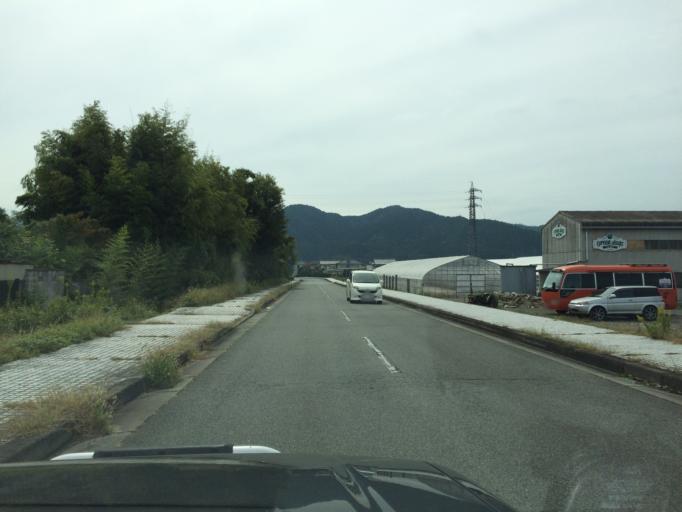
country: JP
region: Hyogo
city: Sasayama
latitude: 35.0734
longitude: 135.2135
